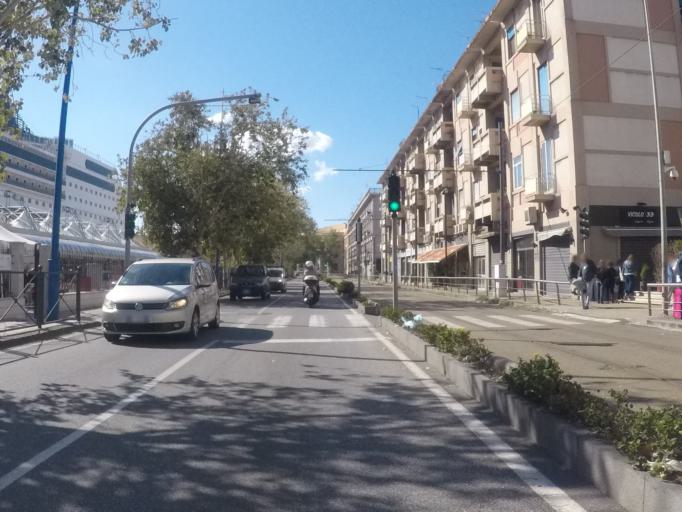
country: IT
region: Sicily
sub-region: Messina
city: Messina
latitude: 38.1921
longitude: 15.5572
